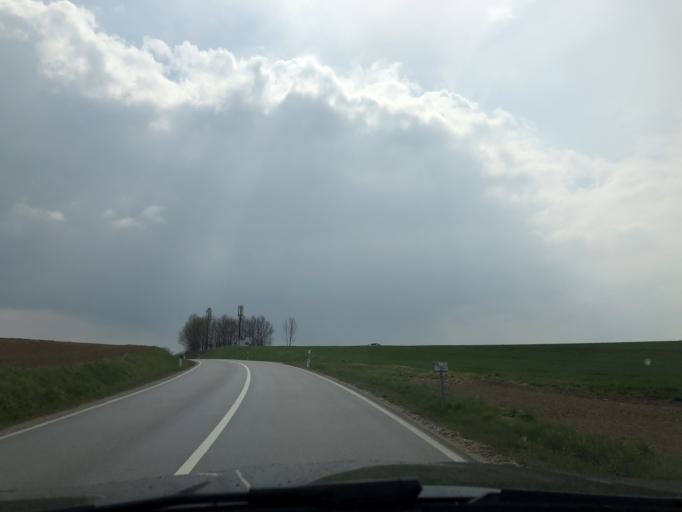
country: DE
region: Bavaria
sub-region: Upper Bavaria
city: Wolfersdorf
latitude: 48.4650
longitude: 11.7052
